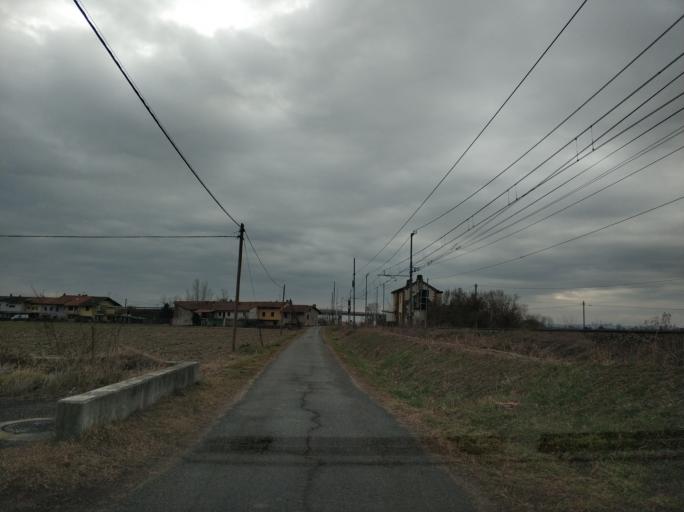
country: IT
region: Piedmont
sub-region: Provincia di Torino
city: Ivrea
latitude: 45.4473
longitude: 7.8850
